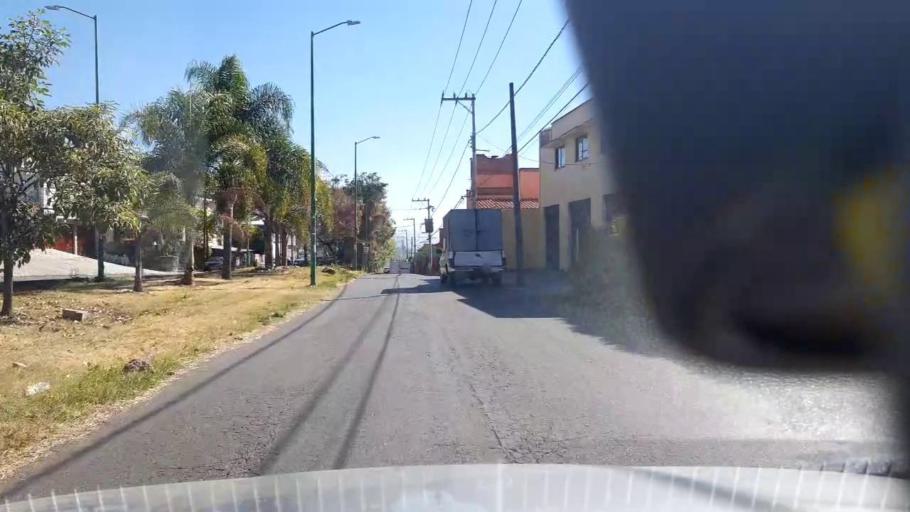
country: MX
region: Morelos
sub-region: Cuernavaca
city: Fraccionamiento Lomas de Ahuatlan
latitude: 18.9637
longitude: -99.2271
